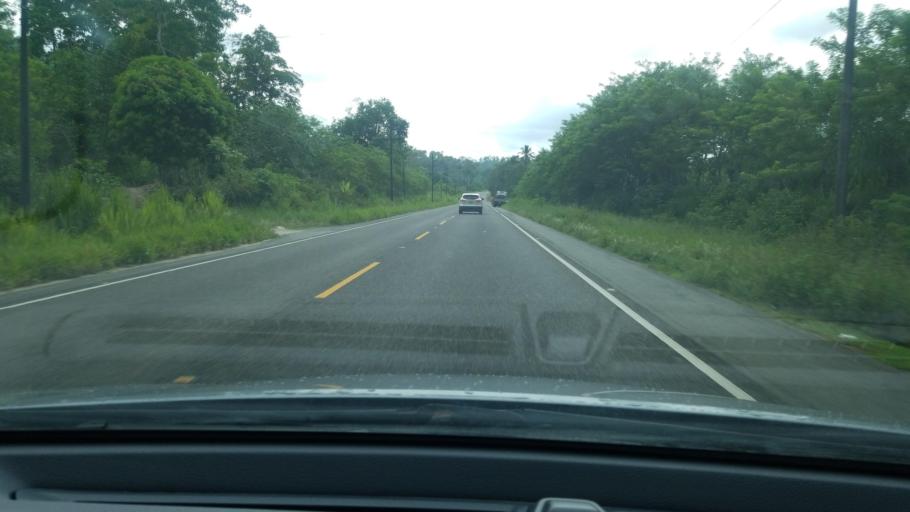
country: HN
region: Cortes
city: Potrerillos
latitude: 15.6141
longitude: -88.2790
